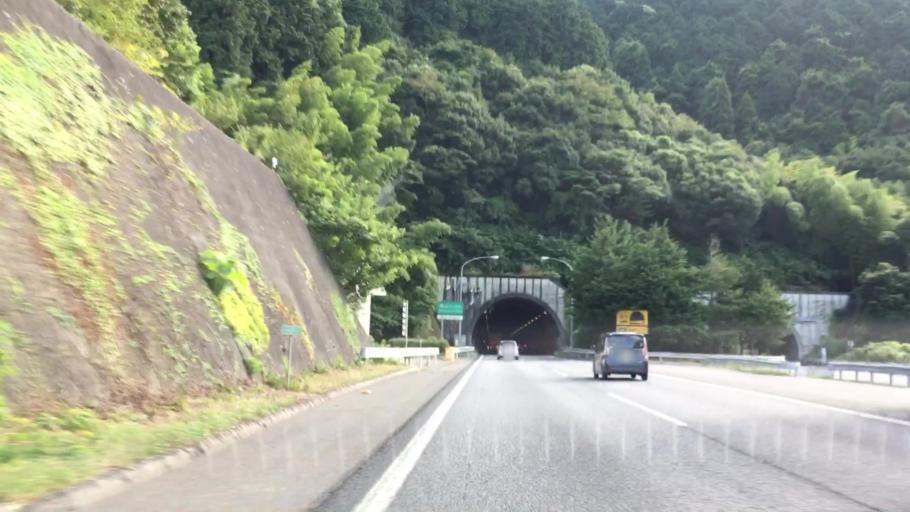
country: JP
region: Yamaguchi
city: Iwakuni
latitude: 34.1671
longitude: 132.1591
